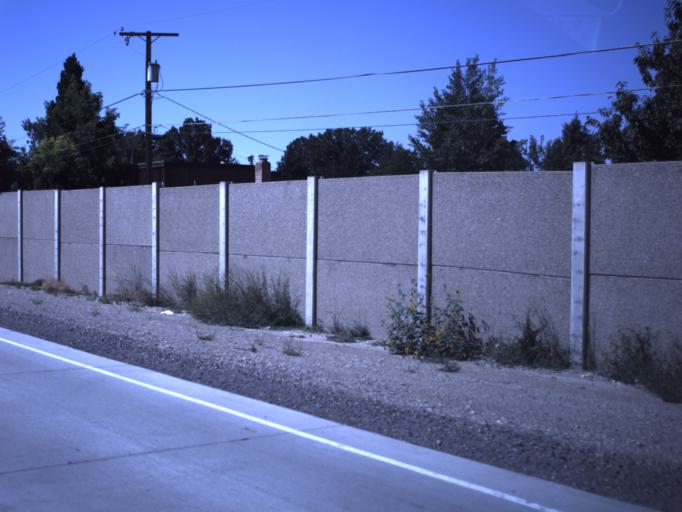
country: US
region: Utah
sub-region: Salt Lake County
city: Taylorsville
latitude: 40.6846
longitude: -111.9517
